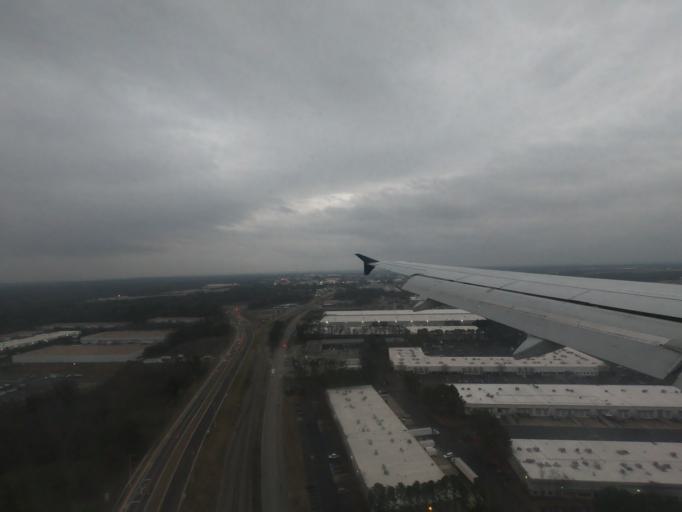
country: US
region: Georgia
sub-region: Fulton County
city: Hapeville
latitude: 33.6492
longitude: -84.3922
